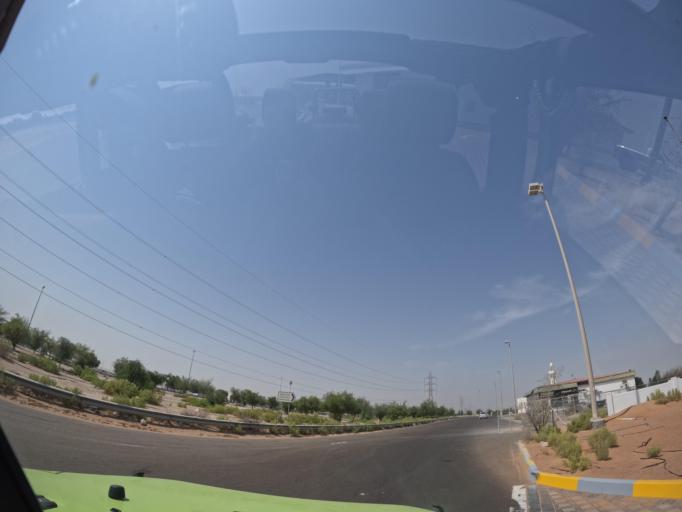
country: AE
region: Abu Dhabi
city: Abu Dhabi
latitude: 24.2194
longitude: 54.8552
